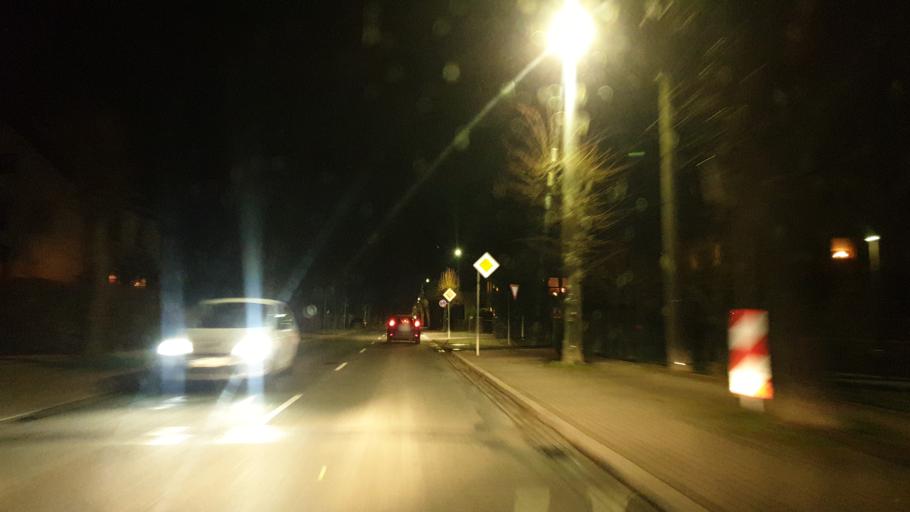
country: DE
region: Saxony
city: Lugau
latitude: 50.7220
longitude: 12.7307
